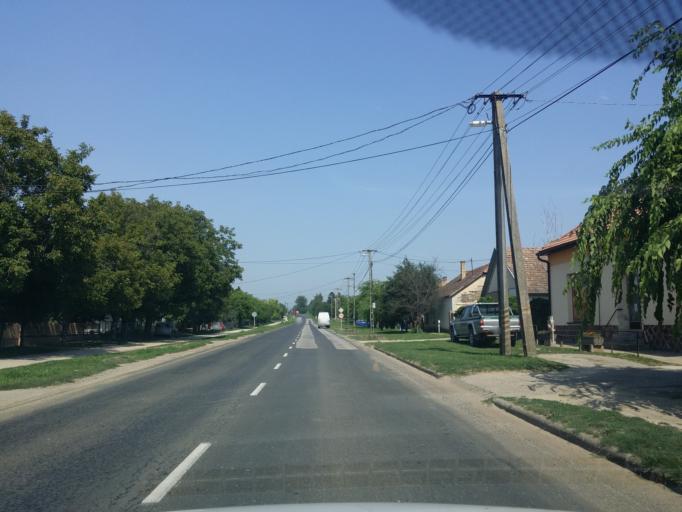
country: HU
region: Tolna
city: Pincehely
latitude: 46.7165
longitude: 18.4784
